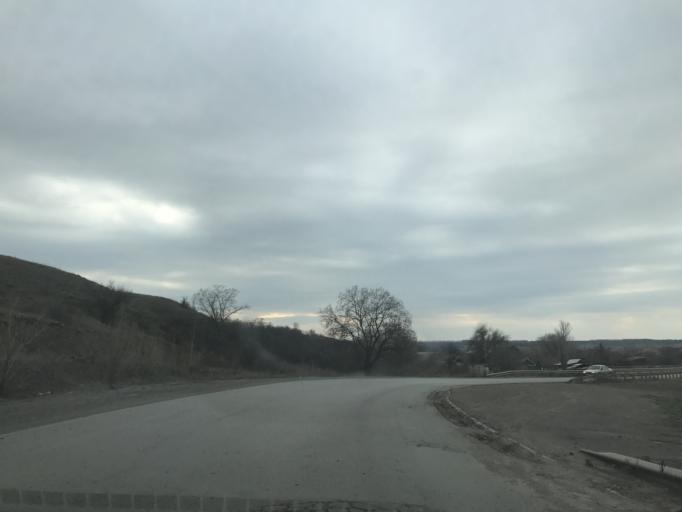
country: RU
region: Rostov
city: Gornyy
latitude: 47.9294
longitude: 40.2942
